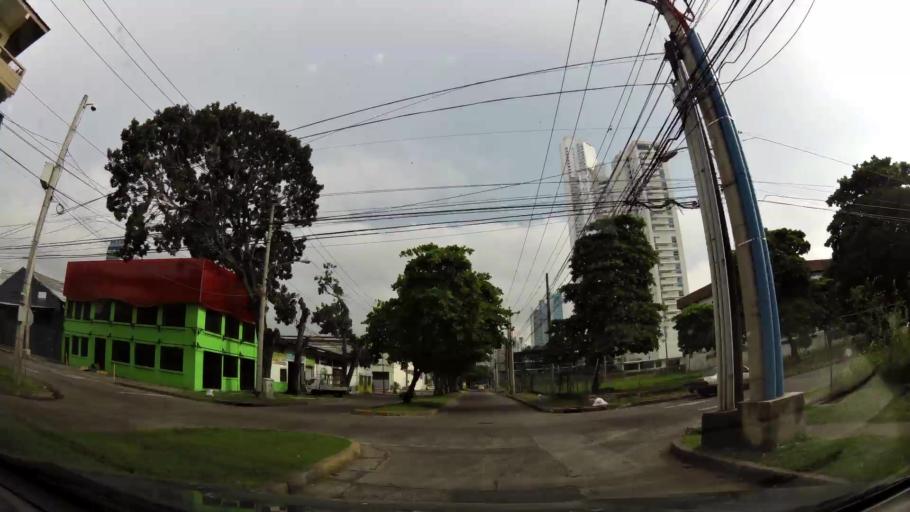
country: PA
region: Panama
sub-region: Distrito de Panama
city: Ancon
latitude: 8.9648
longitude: -79.5360
